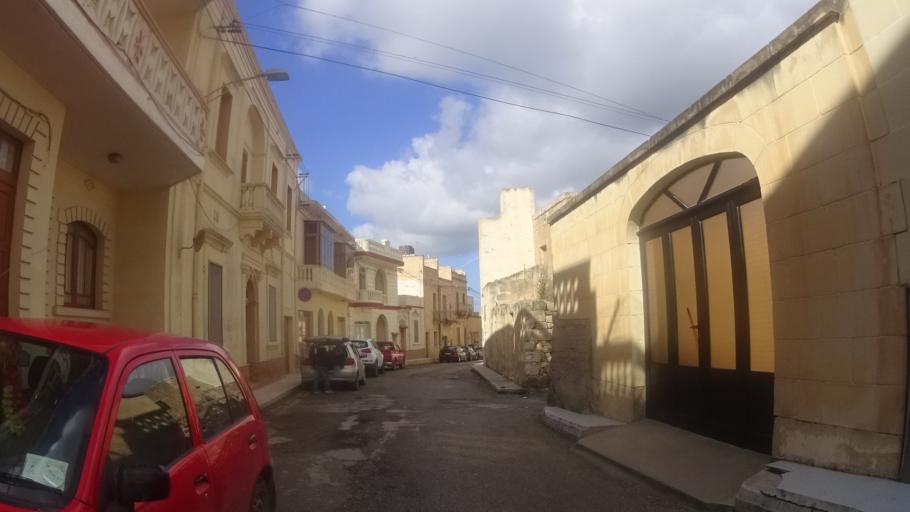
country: MT
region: In-Nadur
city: Nadur
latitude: 36.0398
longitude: 14.2880
